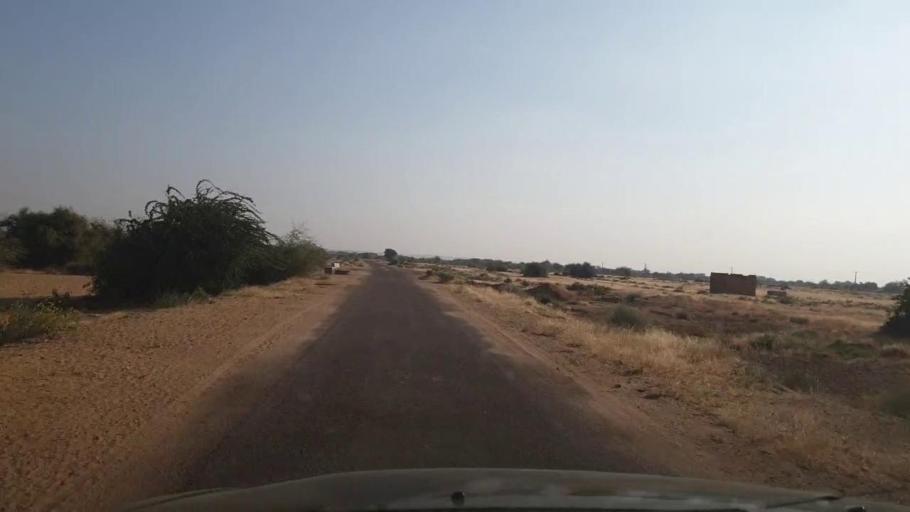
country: PK
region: Sindh
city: Jamshoro
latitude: 25.3439
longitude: 67.8390
